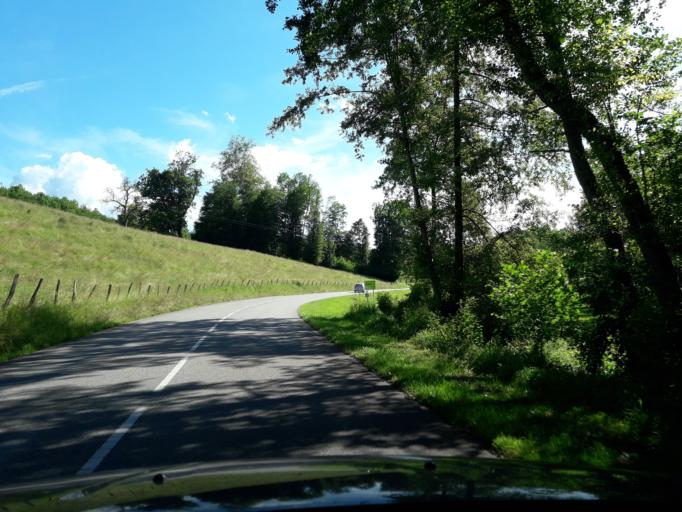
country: FR
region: Rhone-Alpes
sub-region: Departement de la Savoie
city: La Bridoire
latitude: 45.5391
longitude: 5.8015
